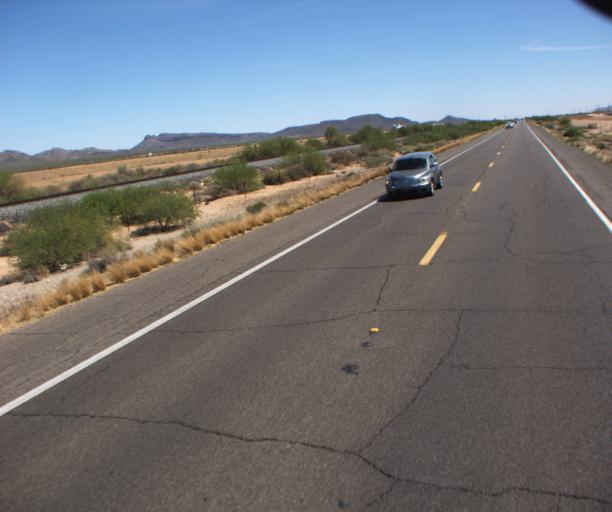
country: US
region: Arizona
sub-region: Pinal County
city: Sacaton
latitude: 33.1583
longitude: -111.7790
